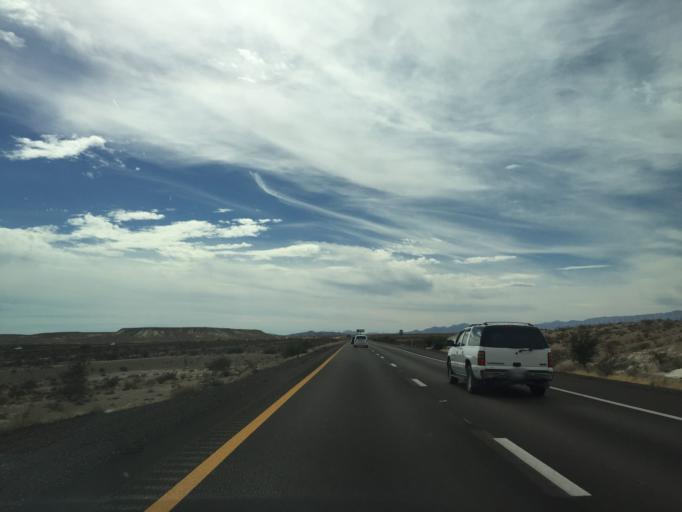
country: US
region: Nevada
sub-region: Clark County
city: Moapa Town
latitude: 36.5518
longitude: -114.6992
